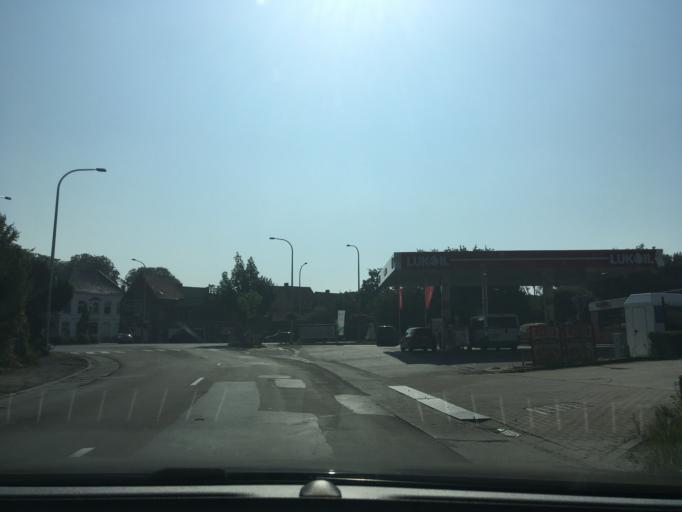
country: BE
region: Flanders
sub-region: Provincie West-Vlaanderen
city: Izegem
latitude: 50.9249
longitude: 3.2156
